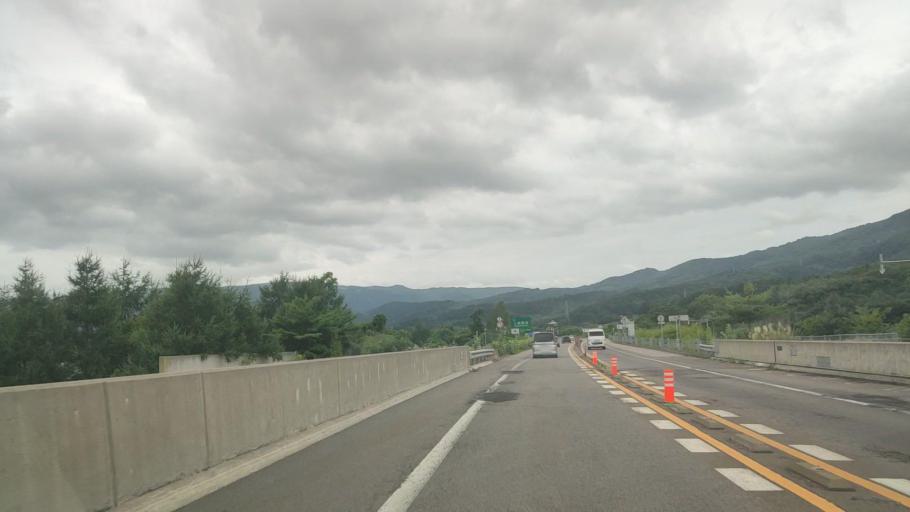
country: JP
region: Hokkaido
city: Nanae
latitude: 41.9176
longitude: 140.6828
